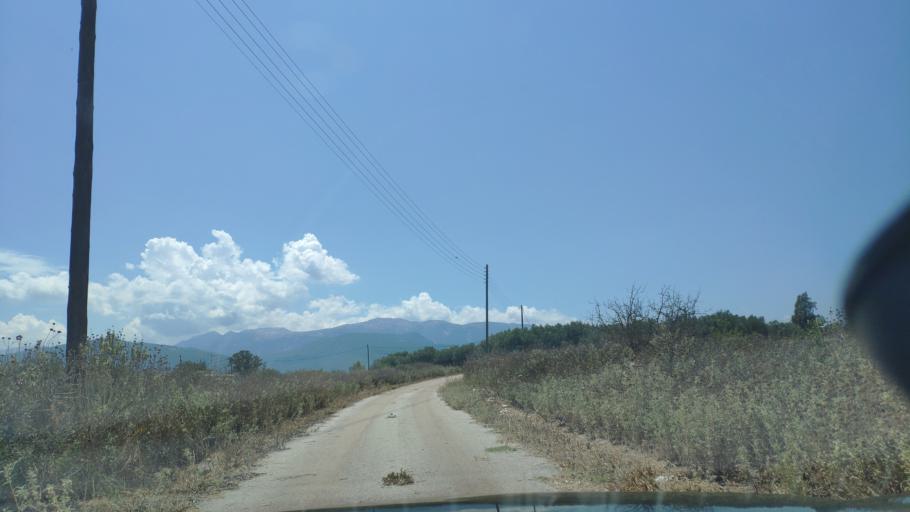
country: GR
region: West Greece
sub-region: Nomos Aitolias kai Akarnanias
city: Amfilochia
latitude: 38.9044
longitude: 21.0942
